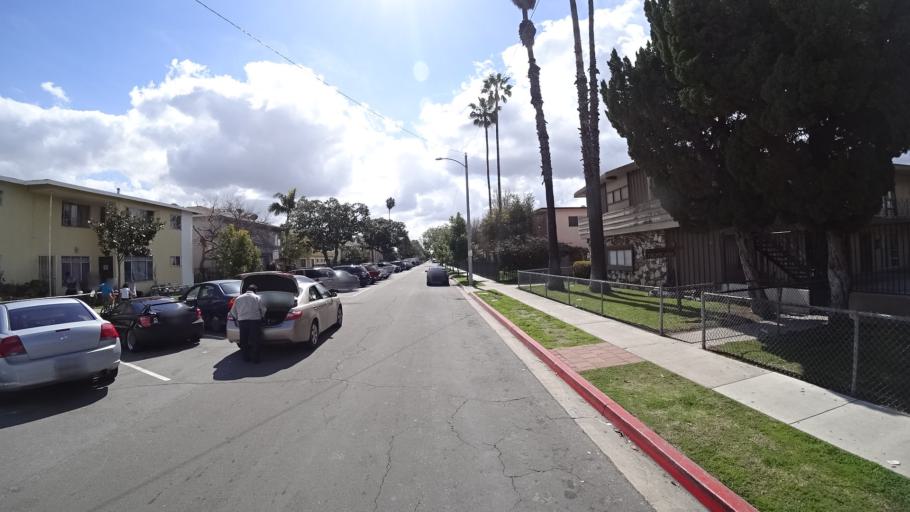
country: US
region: California
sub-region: Orange County
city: Anaheim
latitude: 33.8415
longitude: -117.9059
